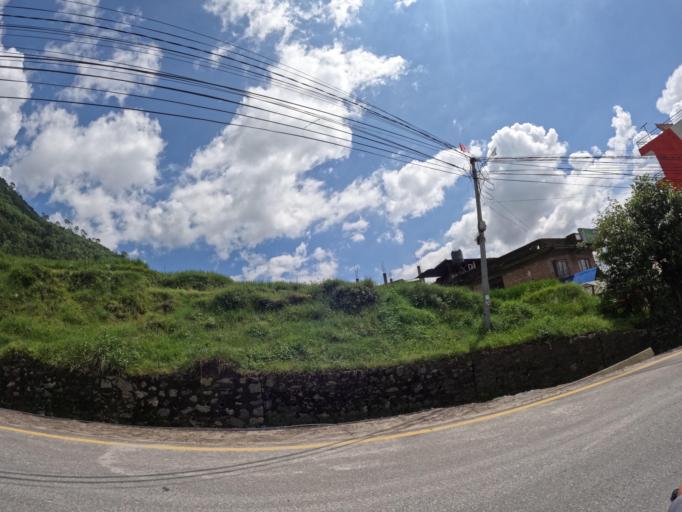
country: NP
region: Central Region
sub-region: Bagmati Zone
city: Kathmandu
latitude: 27.7870
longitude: 85.3296
